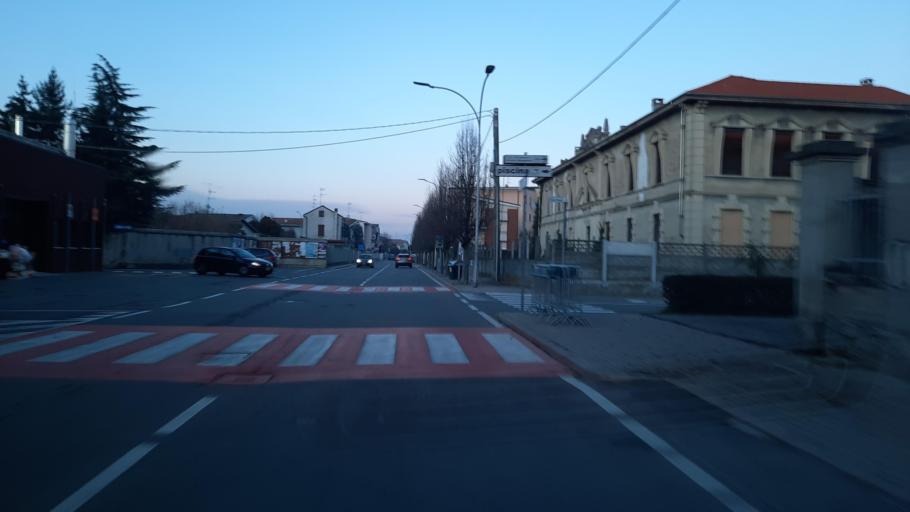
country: IT
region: Piedmont
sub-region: Provincia di Vercelli
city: Trino
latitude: 45.1946
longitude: 8.3005
